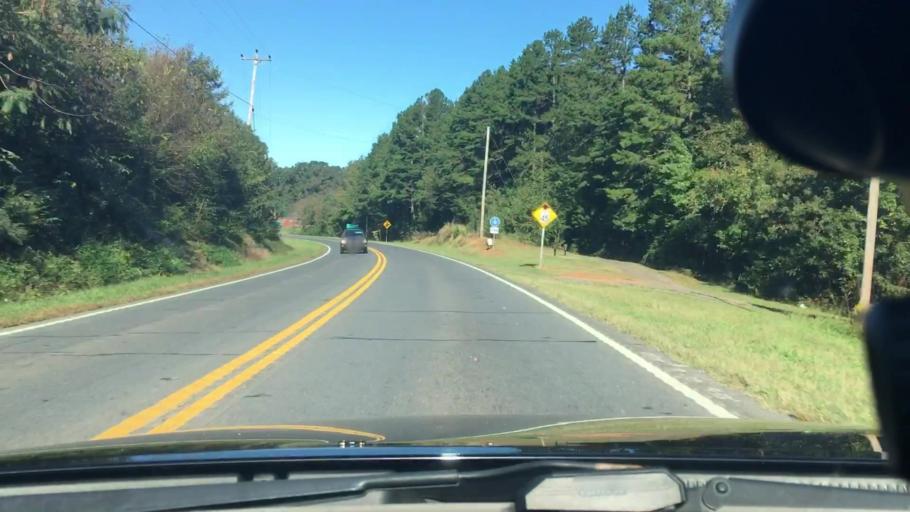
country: US
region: North Carolina
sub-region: Stanly County
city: Albemarle
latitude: 35.3430
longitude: -80.1415
